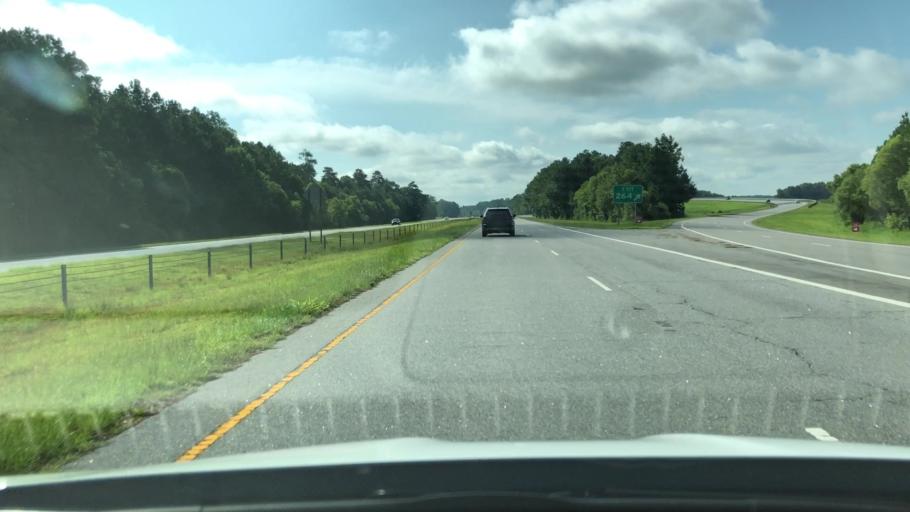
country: US
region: North Carolina
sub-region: Pasquotank County
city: Elizabeth City
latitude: 36.3831
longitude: -76.3143
